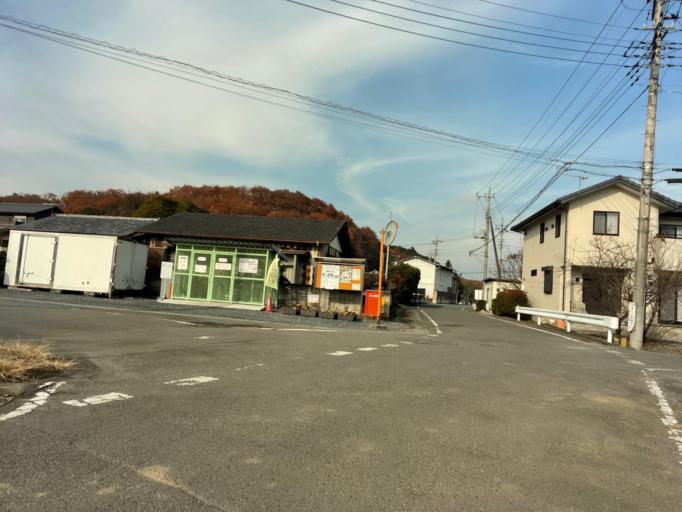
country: JP
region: Saitama
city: Yorii
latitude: 36.1631
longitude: 139.1789
